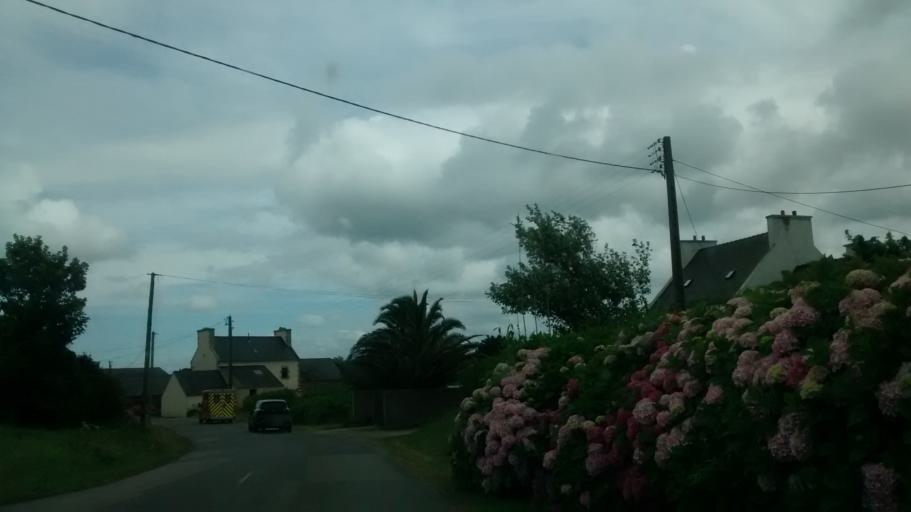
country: FR
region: Brittany
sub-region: Departement du Finistere
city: Guisseny
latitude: 48.6366
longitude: -4.4256
